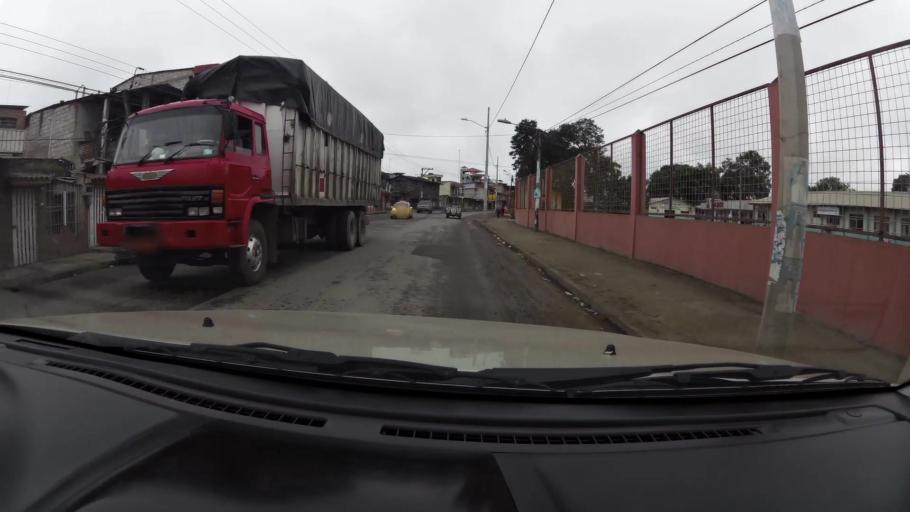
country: EC
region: El Oro
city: Pasaje
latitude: -3.3313
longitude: -79.8126
